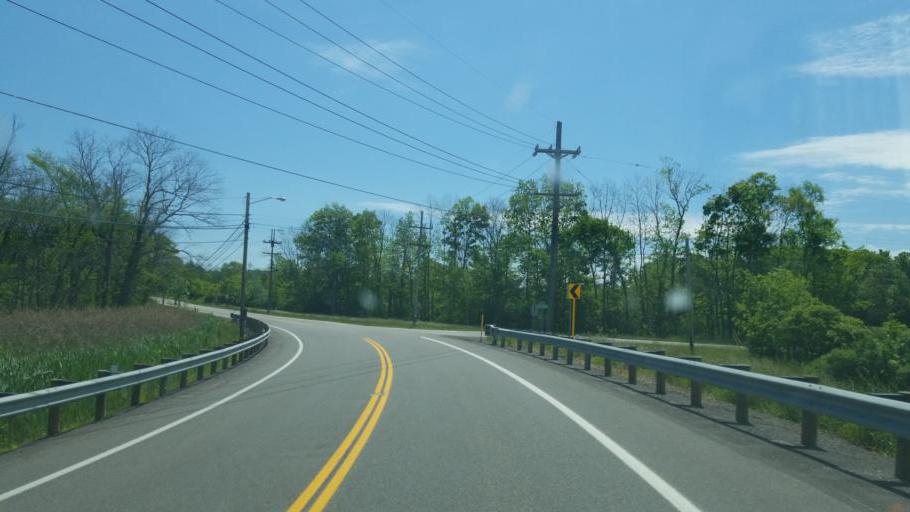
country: US
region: Ohio
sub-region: Geauga County
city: Burton
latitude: 41.4638
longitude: -81.1264
